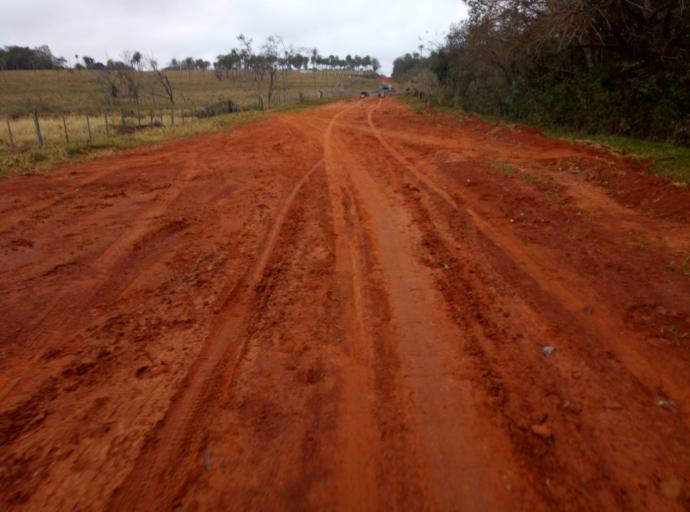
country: PY
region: Caaguazu
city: Doctor Cecilio Baez
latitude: -25.1227
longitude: -56.2095
